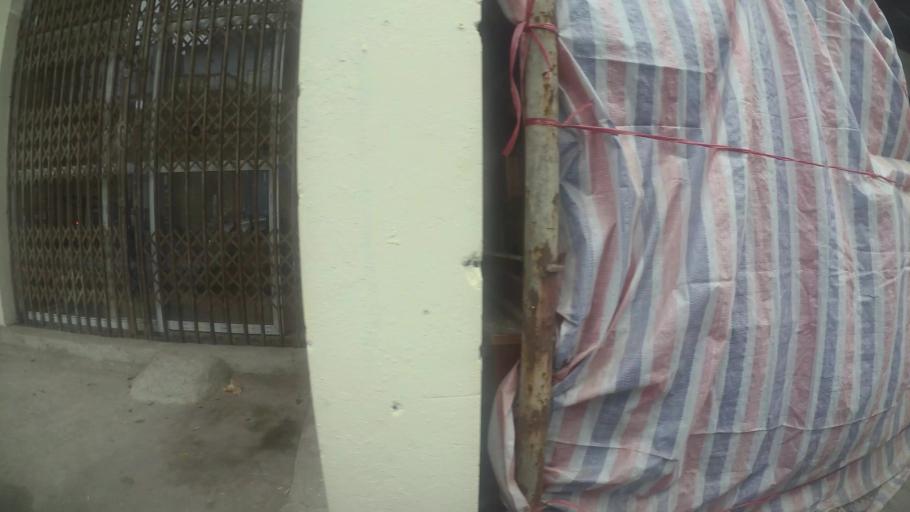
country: VN
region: Ha Noi
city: Tay Ho
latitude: 21.0718
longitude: 105.7900
